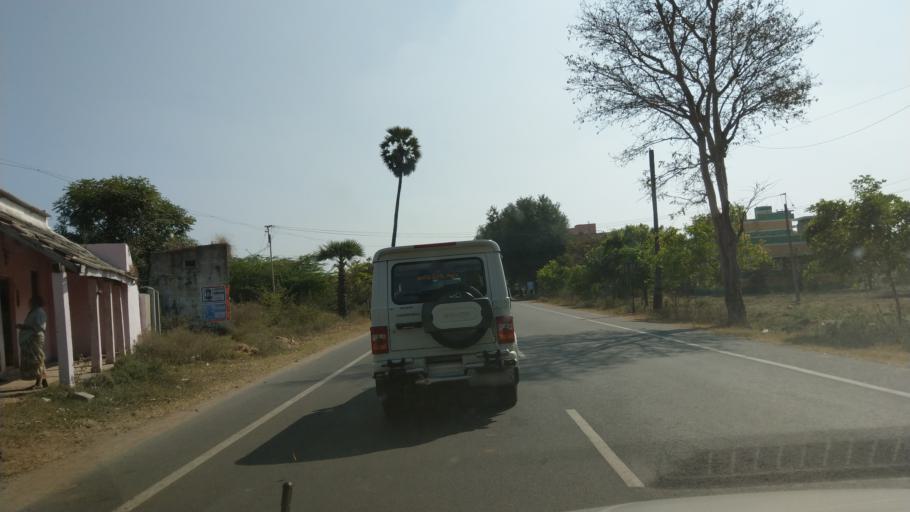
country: IN
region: Tamil Nadu
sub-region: Vellore
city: Arcot
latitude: 12.8783
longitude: 79.3157
